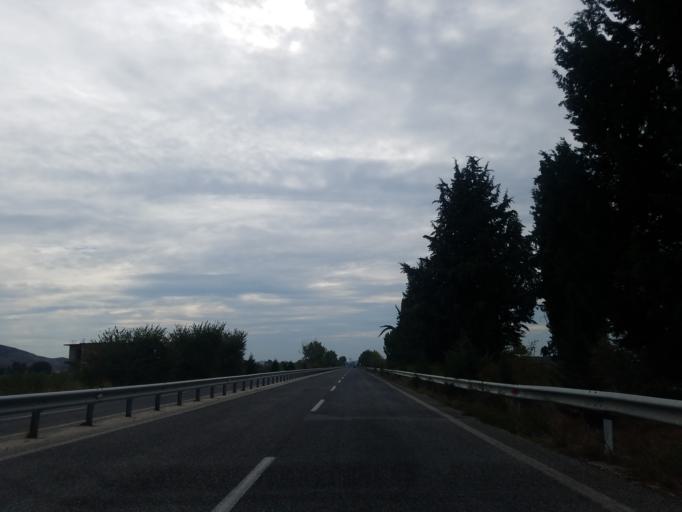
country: GR
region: Thessaly
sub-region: Trikala
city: Vasiliki
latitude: 39.6412
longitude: 21.6932
